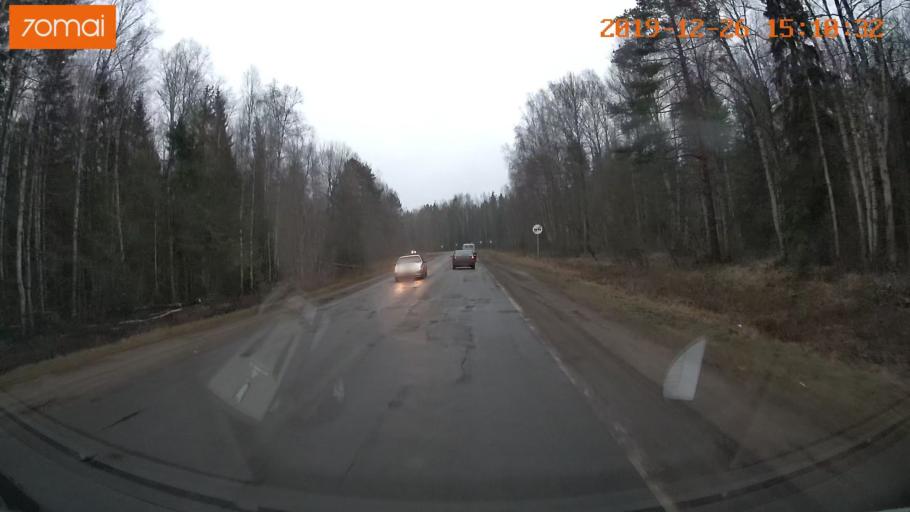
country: RU
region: Jaroslavl
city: Rybinsk
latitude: 58.1397
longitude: 38.8526
